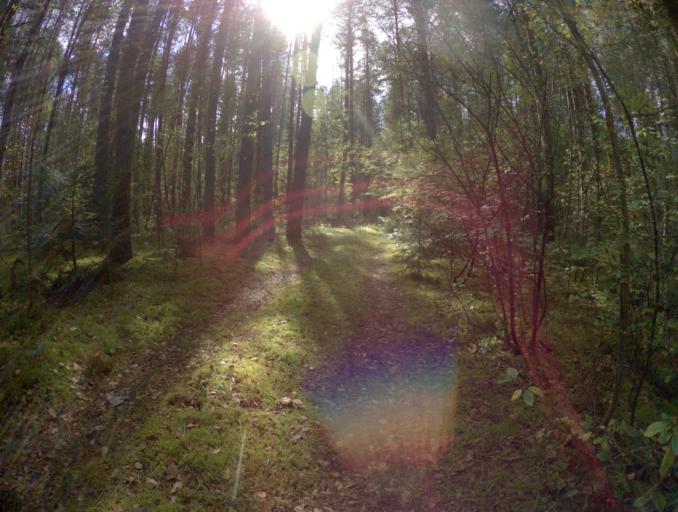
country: RU
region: Vladimir
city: Golovino
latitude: 55.9104
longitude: 40.4337
